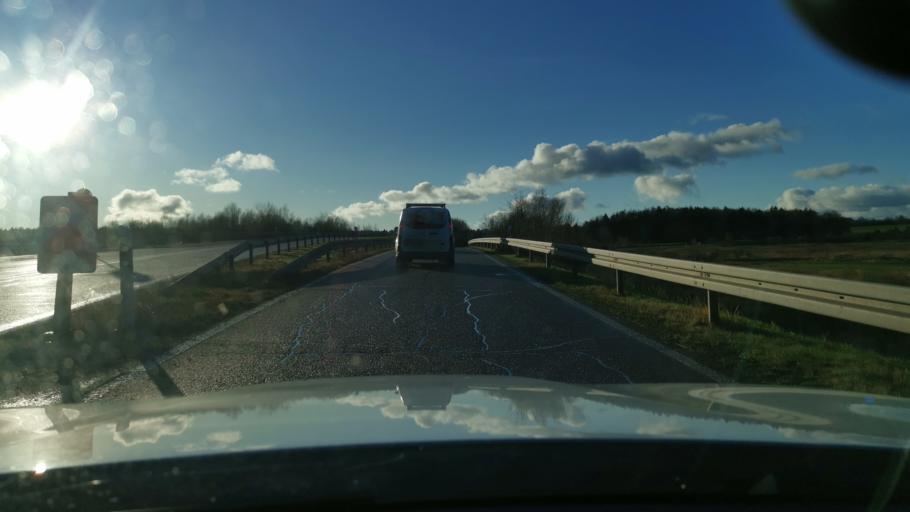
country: DE
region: Mecklenburg-Vorpommern
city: Tessin
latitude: 54.0333
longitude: 12.4107
